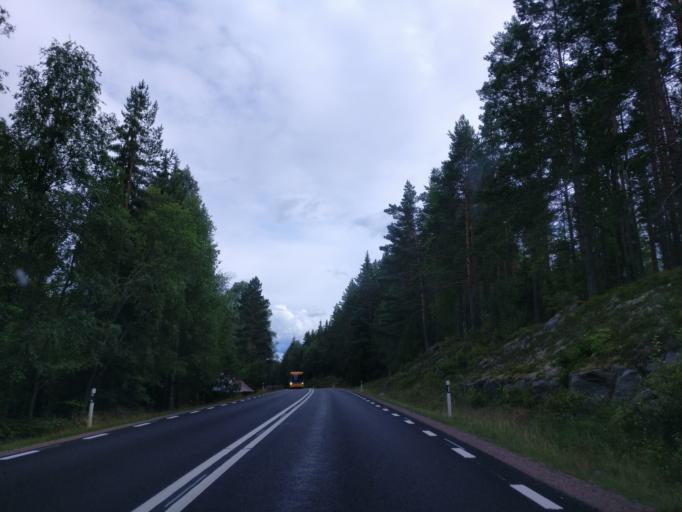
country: SE
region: Vaermland
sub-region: Hagfors Kommun
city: Hagfors
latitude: 60.0565
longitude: 13.5549
